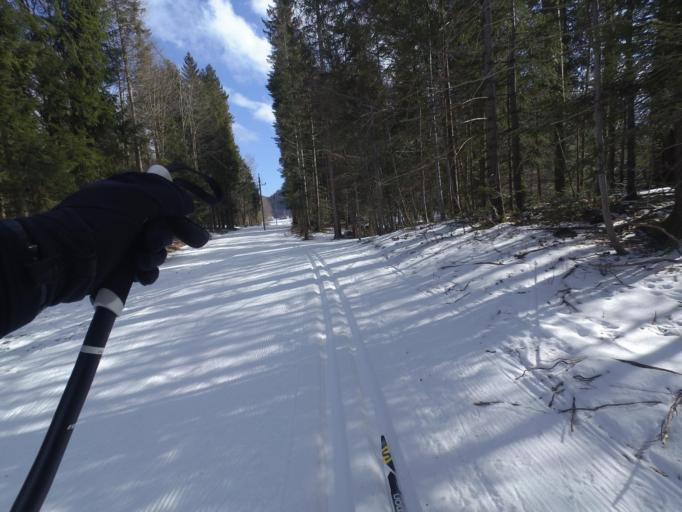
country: AT
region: Salzburg
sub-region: Politischer Bezirk Salzburg-Umgebung
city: Fuschl am See
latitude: 47.7677
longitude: 13.3183
